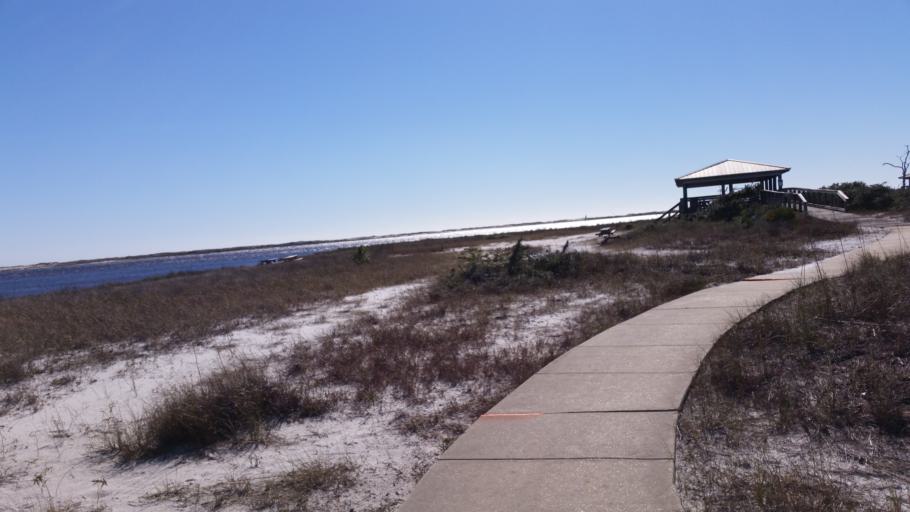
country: US
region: Florida
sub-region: Escambia County
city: Myrtle Grove
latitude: 30.3103
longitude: -87.4003
